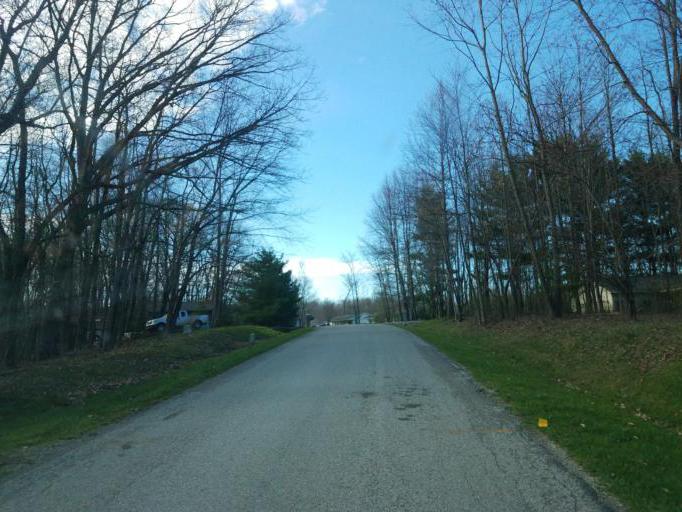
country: US
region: Ohio
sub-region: Knox County
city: Danville
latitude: 40.4470
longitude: -82.3453
